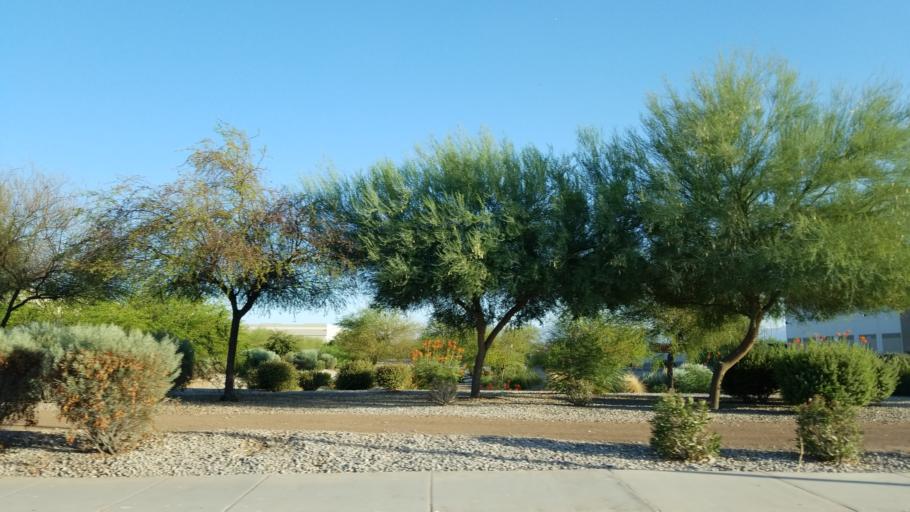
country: US
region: Arizona
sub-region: Maricopa County
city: Laveen
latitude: 33.4224
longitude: -112.1829
